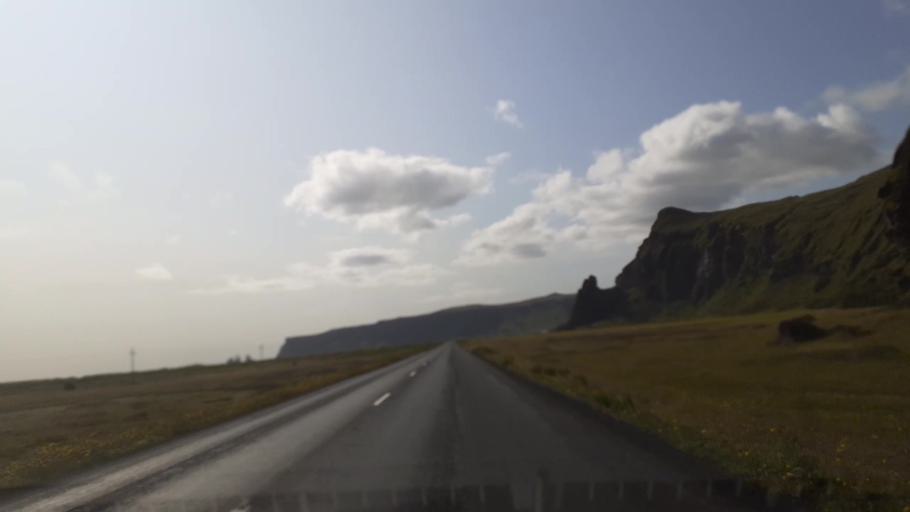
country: IS
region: South
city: Vestmannaeyjar
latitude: 63.4204
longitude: -18.9341
